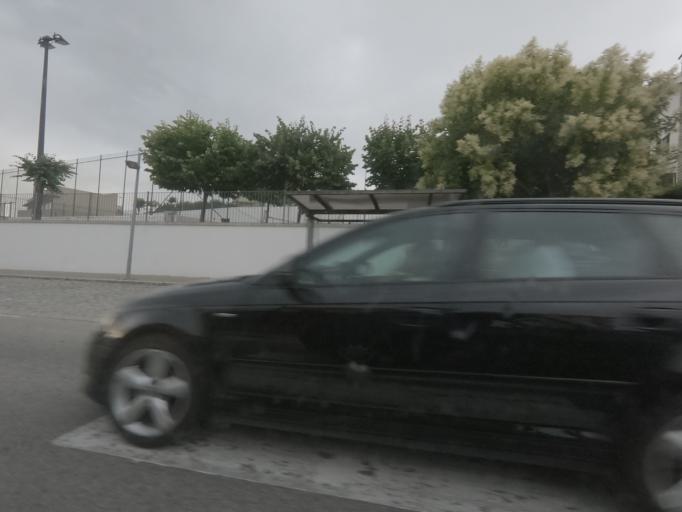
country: PT
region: Viseu
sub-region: Armamar
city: Armamar
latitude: 41.1060
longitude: -7.6913
